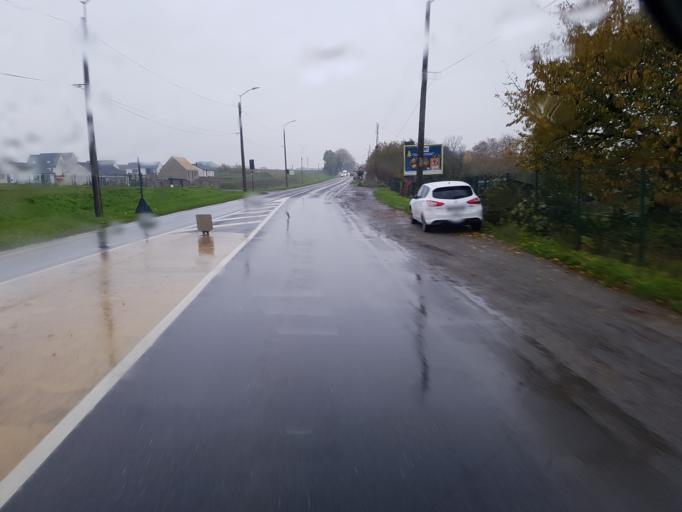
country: FR
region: Picardie
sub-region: Departement de l'Aisne
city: Saint-Quentin
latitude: 49.8654
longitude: 3.2743
